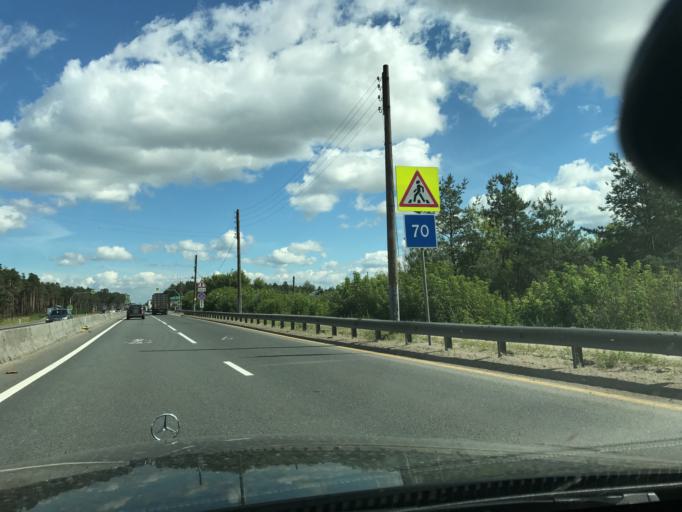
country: RU
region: Nizjnij Novgorod
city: Dzerzhinsk
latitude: 56.2976
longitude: 43.4588
